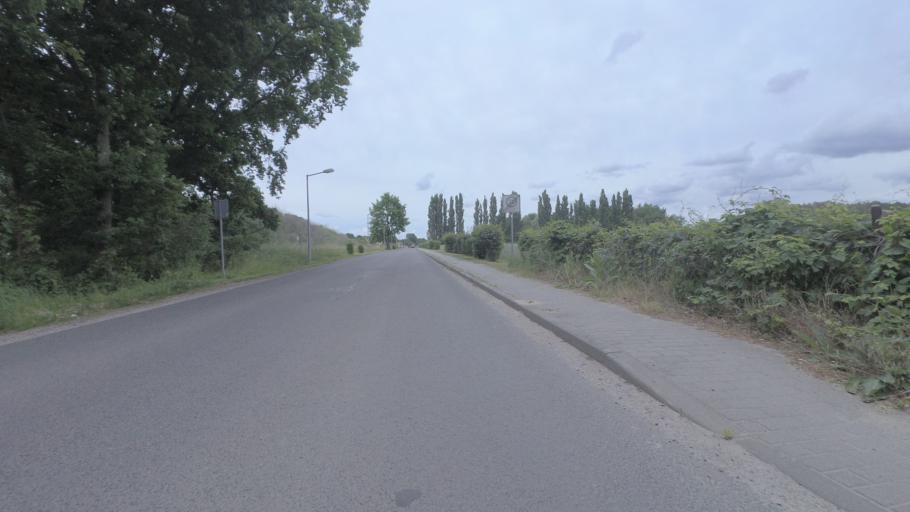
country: DE
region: Brandenburg
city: Bestensee
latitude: 52.2748
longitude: 13.7428
